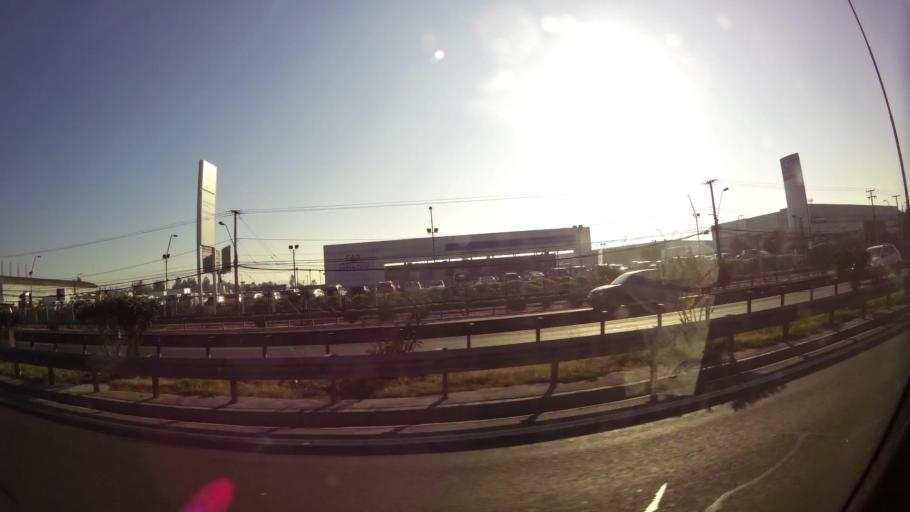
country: CL
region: Santiago Metropolitan
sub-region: Provincia de Santiago
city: Lo Prado
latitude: -33.4495
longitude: -70.7753
